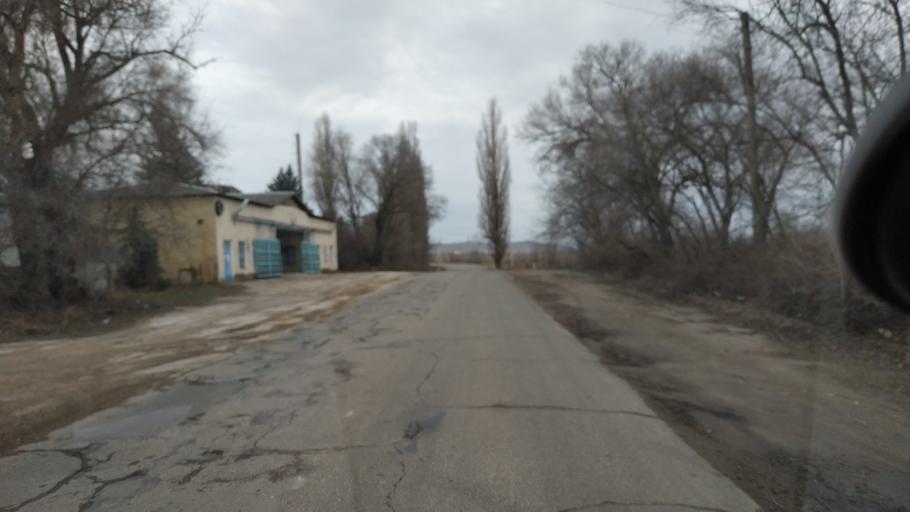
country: MD
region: Criuleni
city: Criuleni
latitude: 47.2394
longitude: 29.1511
